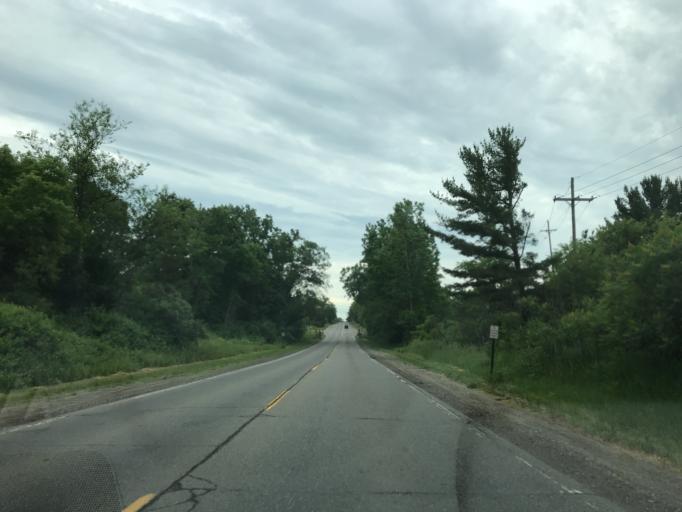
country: US
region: Michigan
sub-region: Oakland County
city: South Lyon
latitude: 42.5151
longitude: -83.6898
